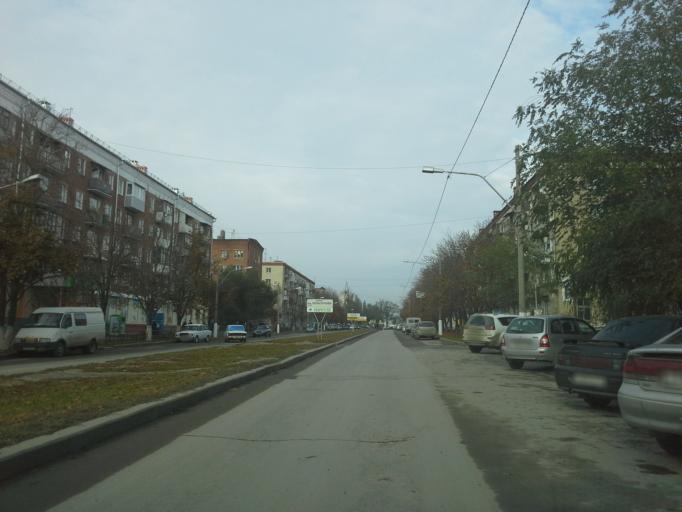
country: RU
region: Volgograd
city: Vodstroy
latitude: 48.7824
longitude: 44.5672
